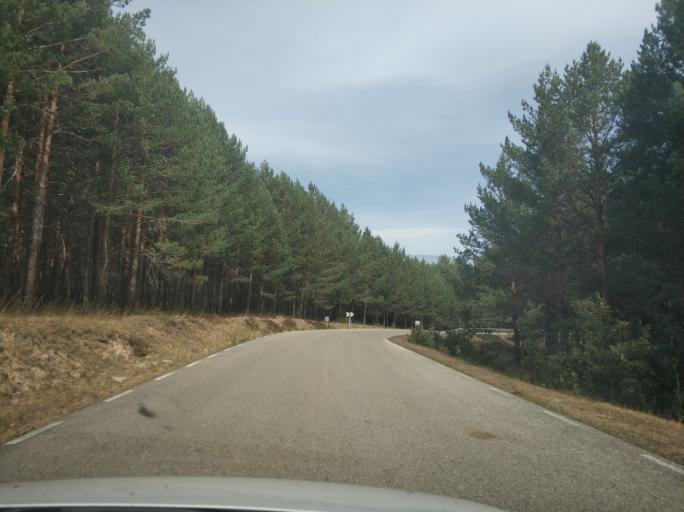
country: ES
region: Castille and Leon
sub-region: Provincia de Soria
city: Duruelo de la Sierra
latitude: 41.8785
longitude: -2.9378
